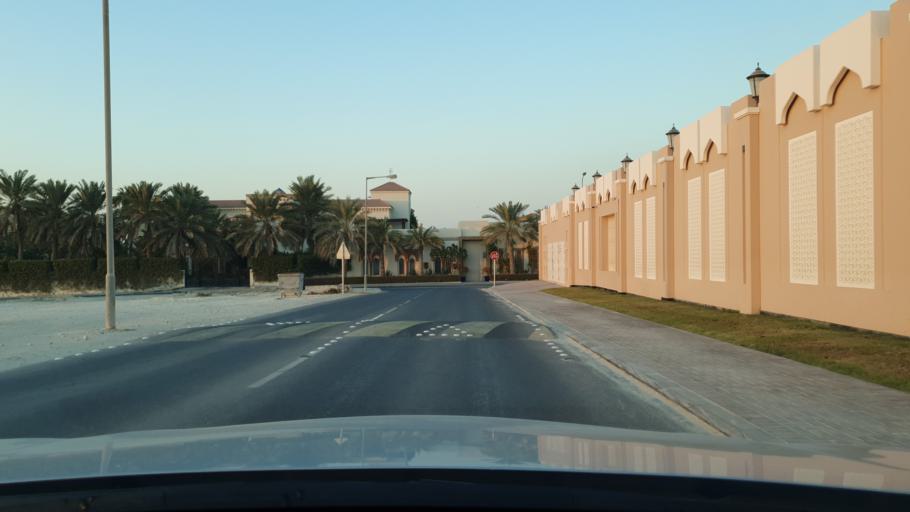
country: BH
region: Northern
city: Ar Rifa'
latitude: 26.1406
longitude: 50.5313
